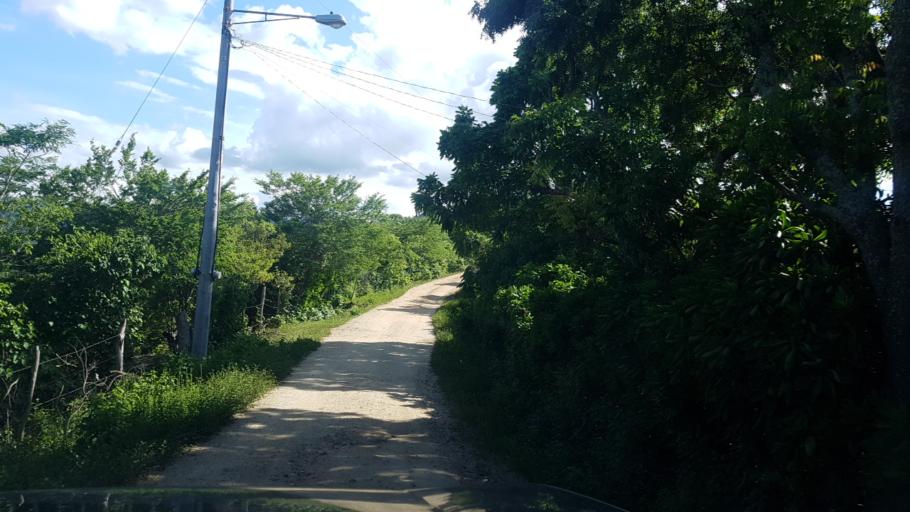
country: NI
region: Nueva Segovia
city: Mozonte
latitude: 13.6362
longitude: -86.3985
